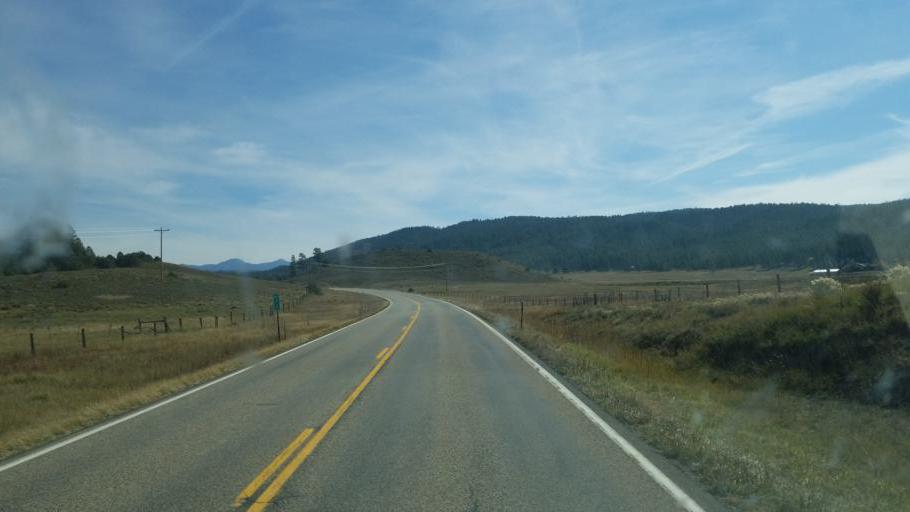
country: US
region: New Mexico
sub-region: Rio Arriba County
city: Dulce
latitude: 37.0806
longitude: -106.8907
